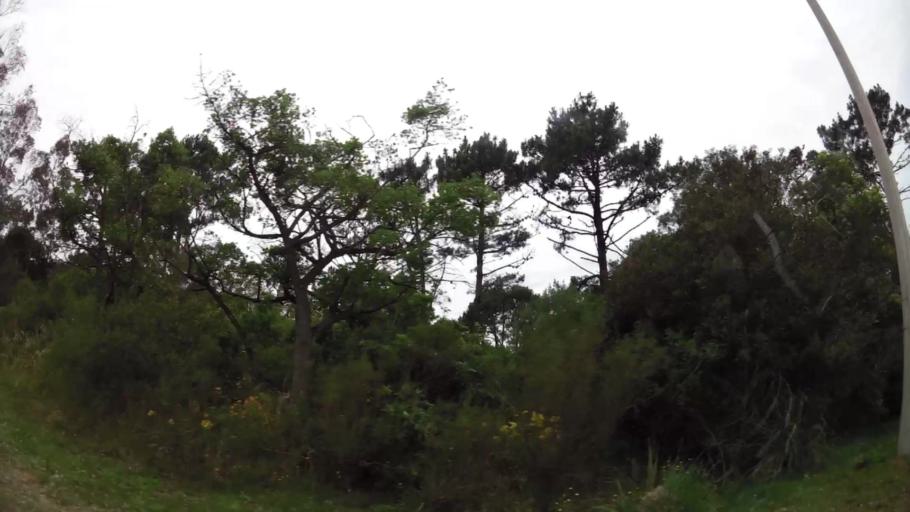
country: UY
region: Maldonado
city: Maldonado
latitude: -34.9001
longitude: -55.0394
